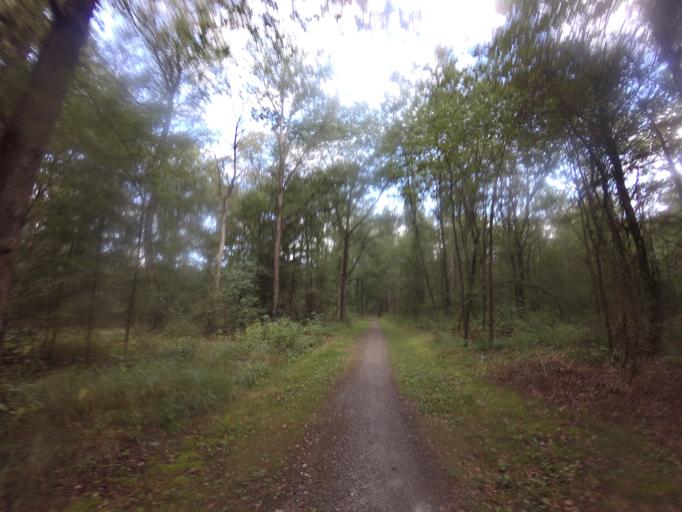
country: NL
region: Overijssel
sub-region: Gemeente Staphorst
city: Staphorst
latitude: 52.6483
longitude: 6.2656
